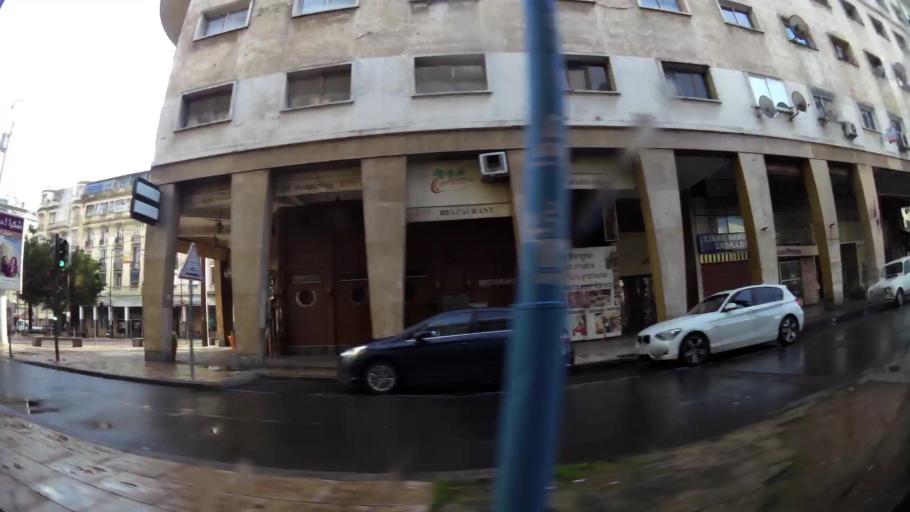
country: MA
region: Grand Casablanca
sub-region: Casablanca
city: Casablanca
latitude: 33.5934
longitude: -7.6087
